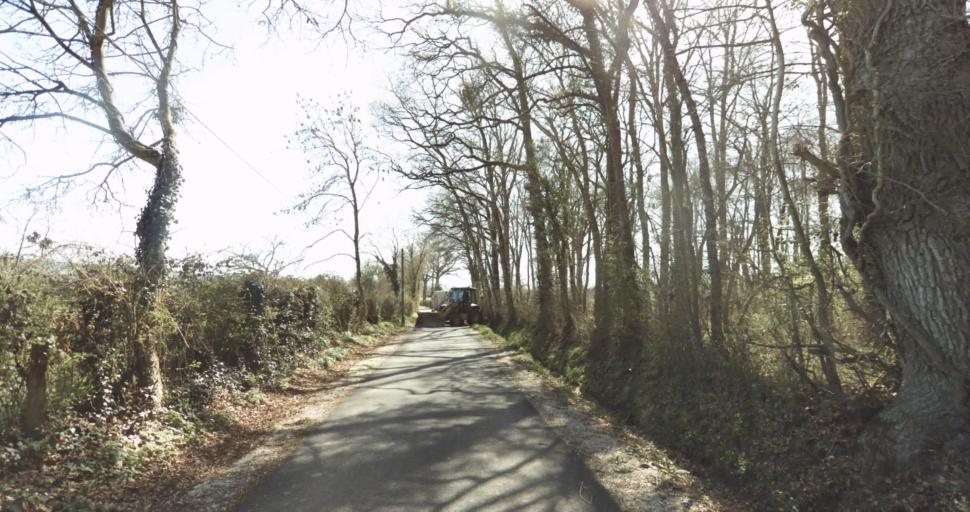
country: FR
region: Lower Normandy
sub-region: Departement du Calvados
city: Saint-Pierre-sur-Dives
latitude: 49.0082
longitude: -0.0008
